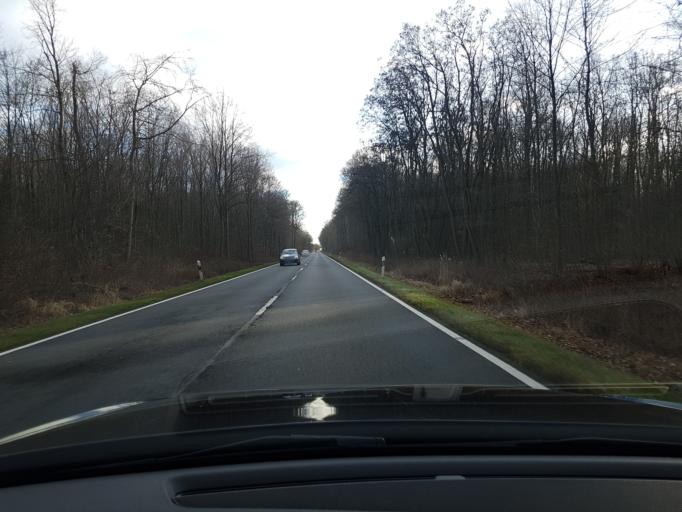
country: DE
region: Brandenburg
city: Gransee
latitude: 53.0677
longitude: 13.1836
